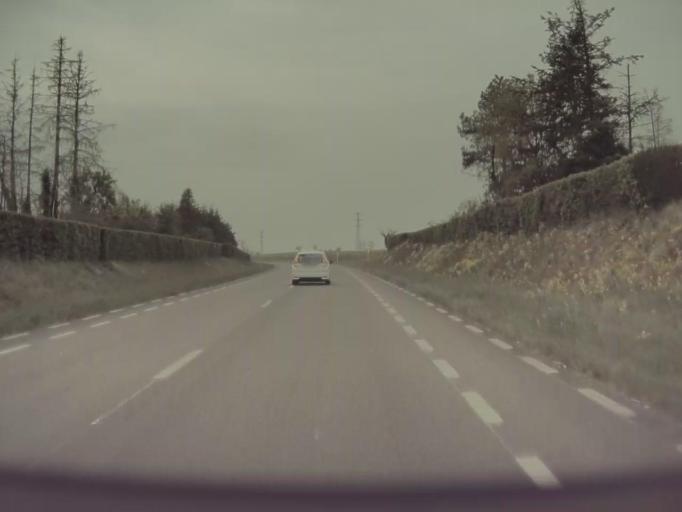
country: BE
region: Wallonia
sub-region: Province de Liege
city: Hamoir
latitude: 50.3956
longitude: 5.4938
